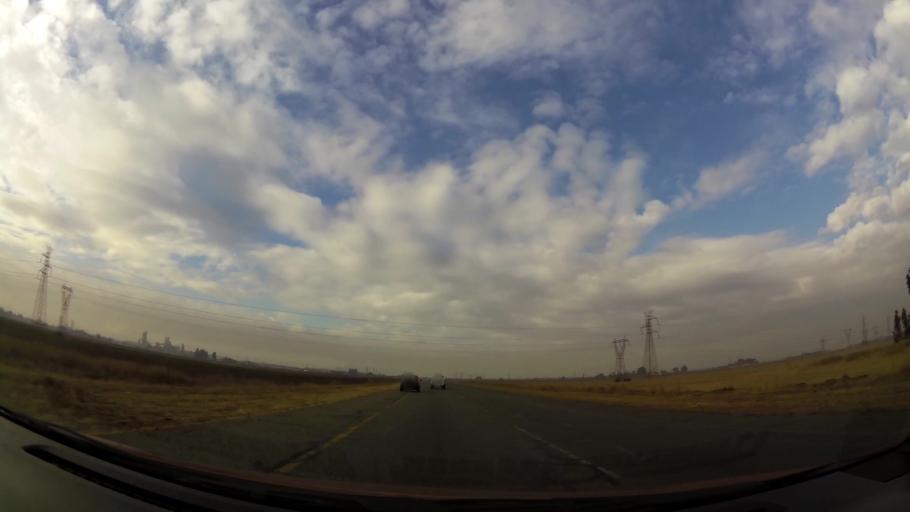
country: ZA
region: Gauteng
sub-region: Sedibeng District Municipality
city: Vanderbijlpark
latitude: -26.6653
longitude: 27.7871
